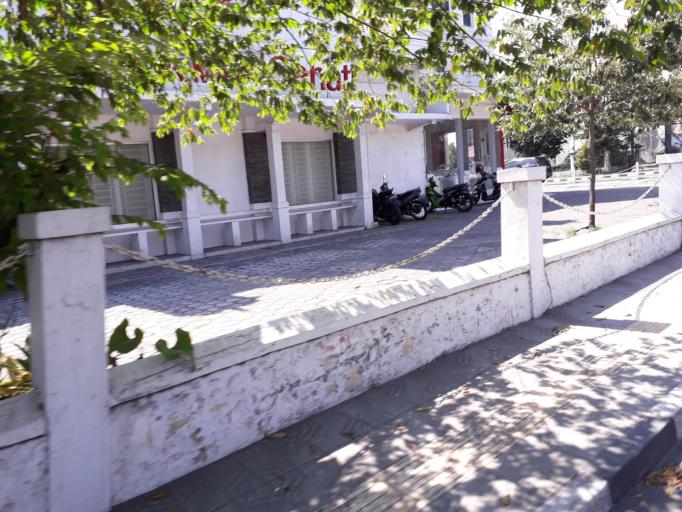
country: ID
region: Daerah Istimewa Yogyakarta
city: Yogyakarta
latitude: -7.7889
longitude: 110.3740
